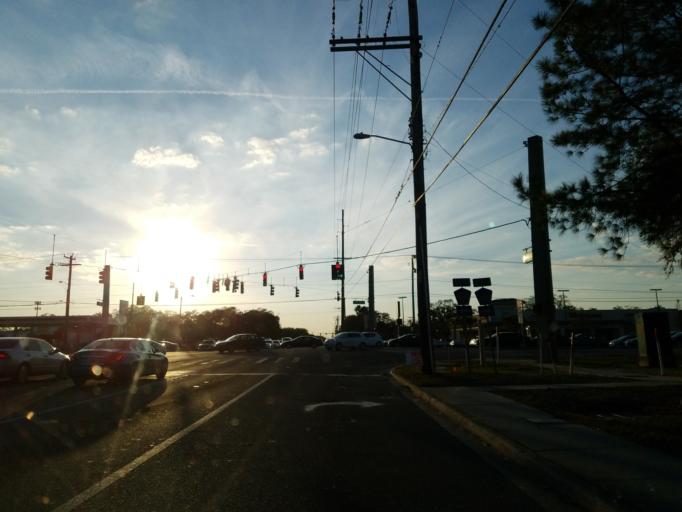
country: US
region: Florida
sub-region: Hillsborough County
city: University
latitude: 28.0693
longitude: -82.4255
